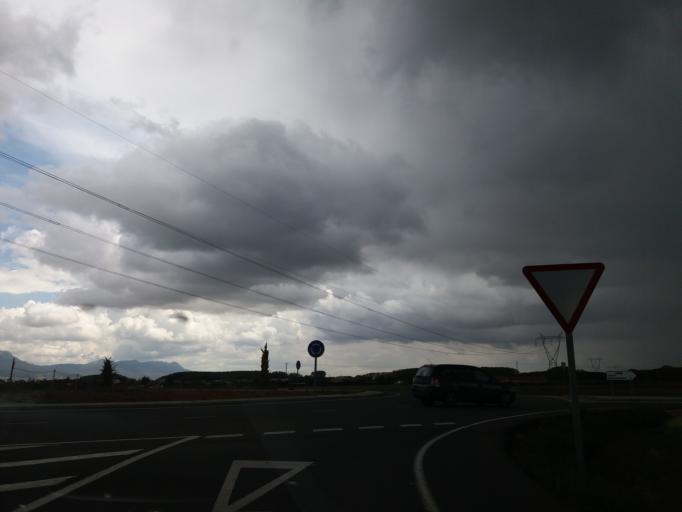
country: ES
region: La Rioja
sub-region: Provincia de La Rioja
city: Cihuri
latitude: 42.5745
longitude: -2.9196
